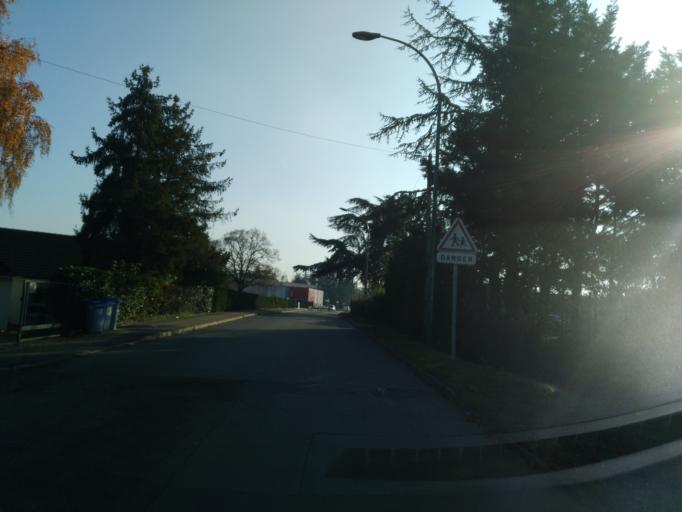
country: FR
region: Ile-de-France
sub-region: Departement des Yvelines
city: Plaisir
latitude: 48.8284
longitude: 1.9365
